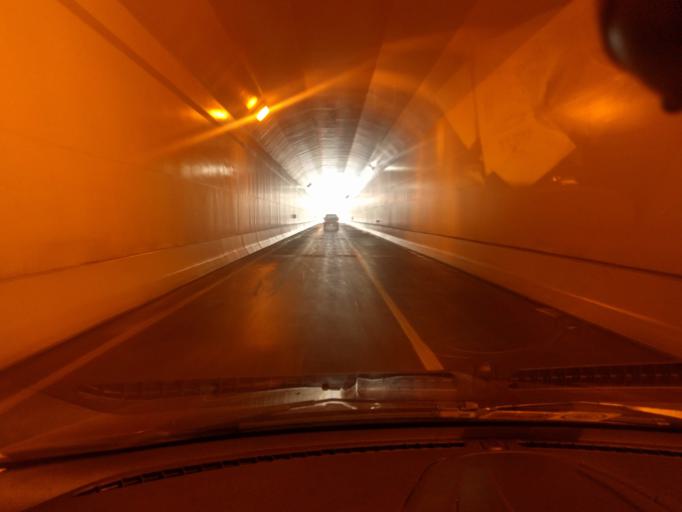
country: US
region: Virginia
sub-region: Roanoke County
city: Hollins
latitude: 37.3329
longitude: -79.9672
